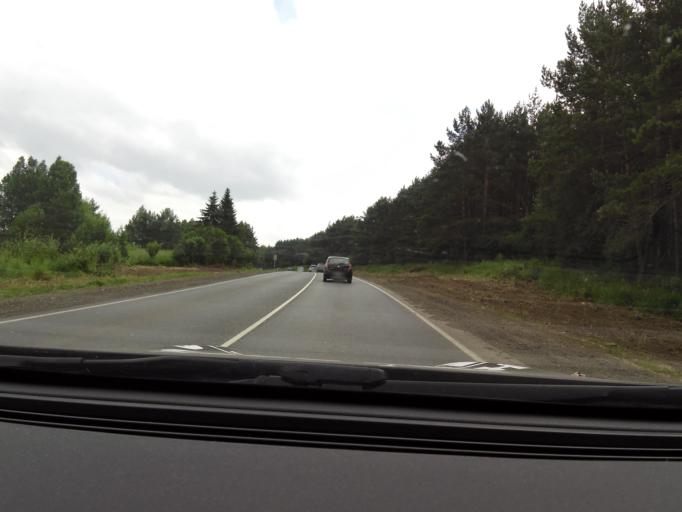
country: RU
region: Perm
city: Kungur
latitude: 57.4549
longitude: 56.7690
